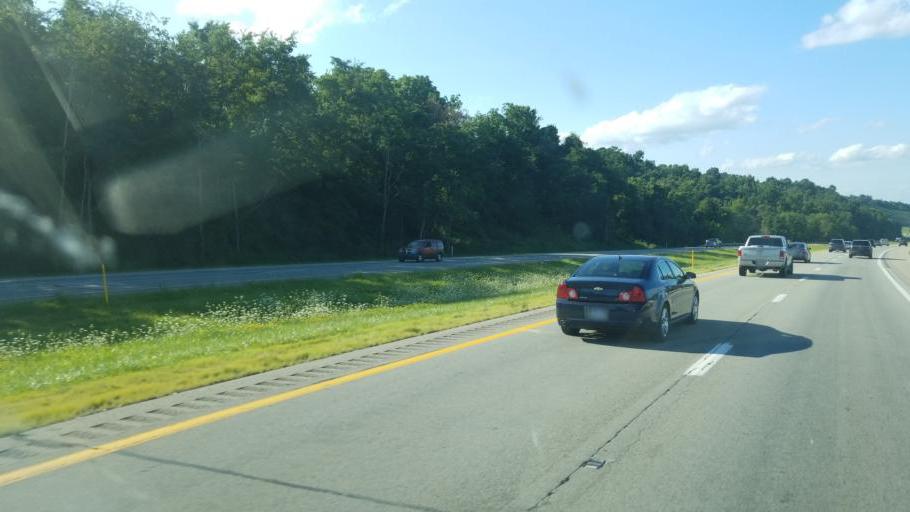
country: US
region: Pennsylvania
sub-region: Greene County
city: Morrisville
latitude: 39.8779
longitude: -80.1332
